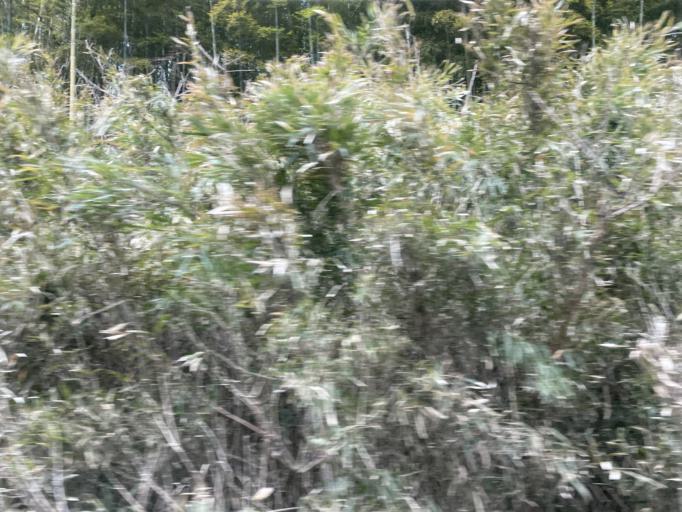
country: JP
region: Chiba
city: Narita
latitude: 35.8015
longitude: 140.2895
